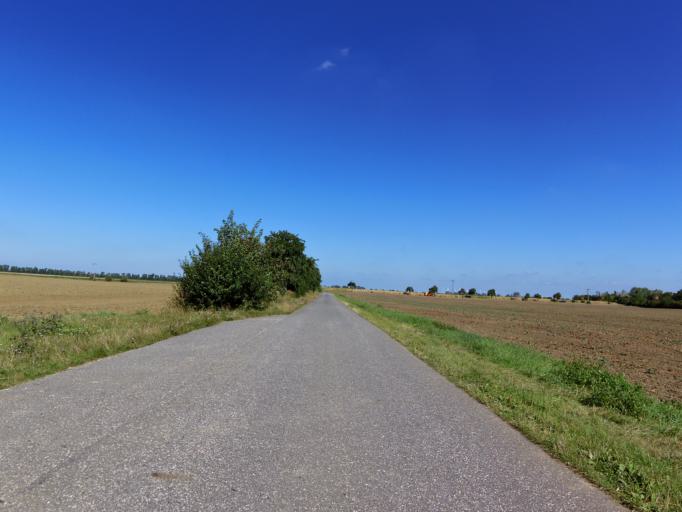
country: DE
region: Brandenburg
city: Muhlberg
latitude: 51.4014
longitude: 13.2433
